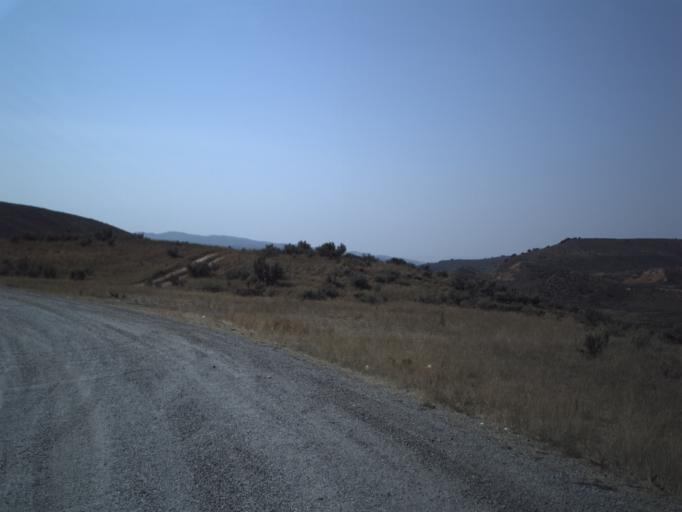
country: US
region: Wyoming
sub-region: Uinta County
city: Evanston
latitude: 41.1208
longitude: -111.1922
